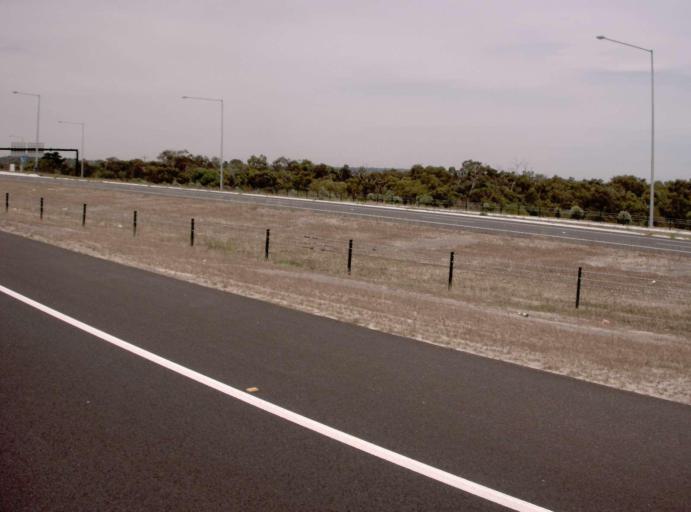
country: AU
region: Victoria
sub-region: Frankston
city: Carrum Downs
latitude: -38.1060
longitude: 145.1602
